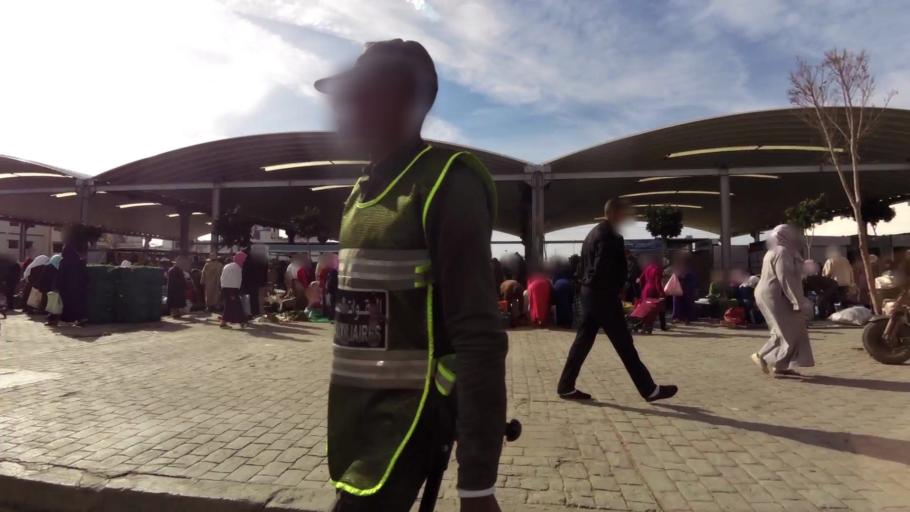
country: MA
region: Tanger-Tetouan
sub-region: Tanger-Assilah
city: Tangier
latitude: 35.7575
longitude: -5.7905
